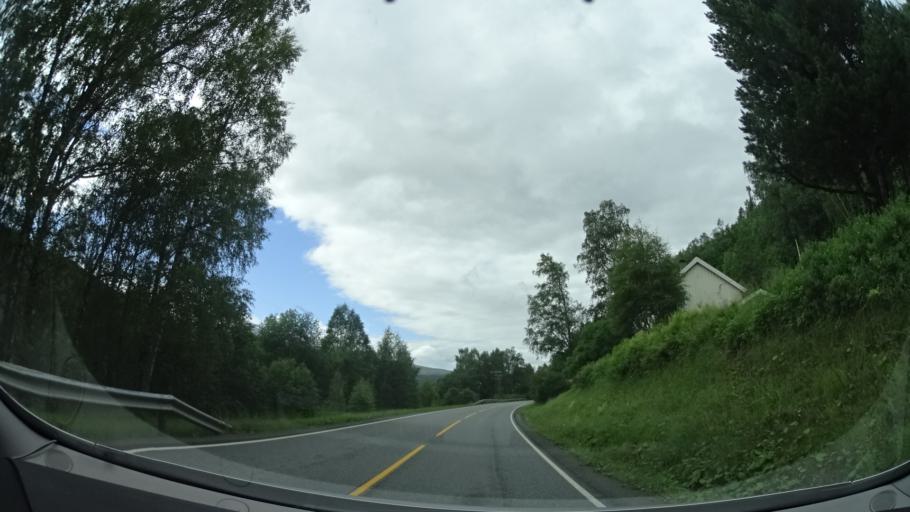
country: NO
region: Nord-Trondelag
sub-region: Meraker
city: Meraker
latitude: 63.4037
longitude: 11.7714
